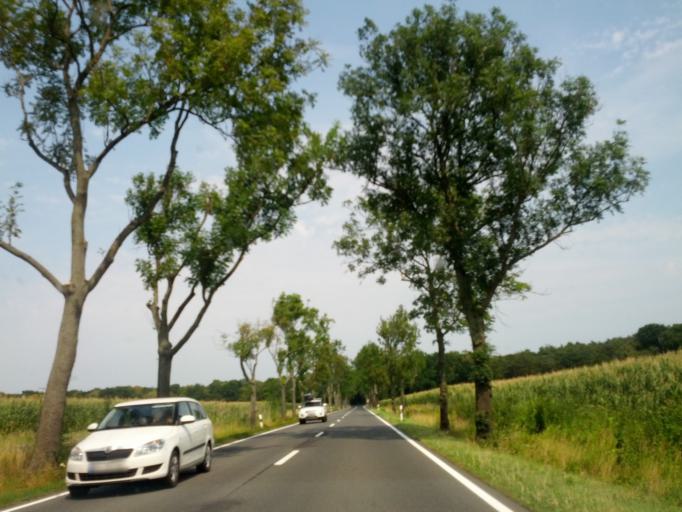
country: DE
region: Brandenburg
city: Nauen
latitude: 52.6390
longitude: 12.9166
